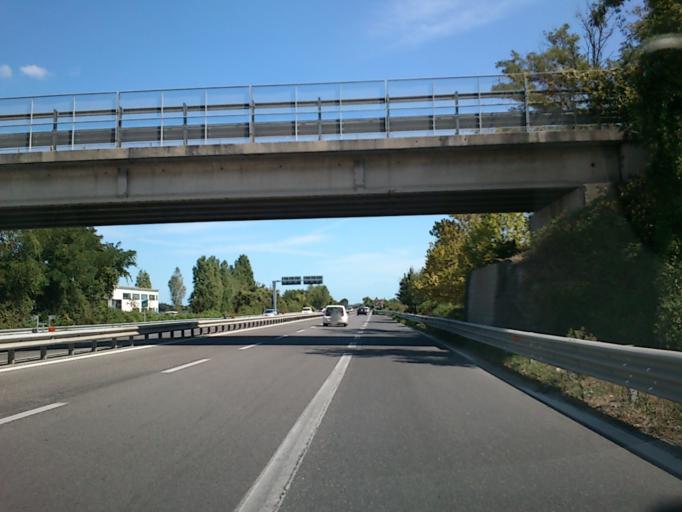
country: IT
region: The Marches
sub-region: Provincia di Pesaro e Urbino
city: Lucrezia
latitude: 43.7690
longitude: 12.9580
